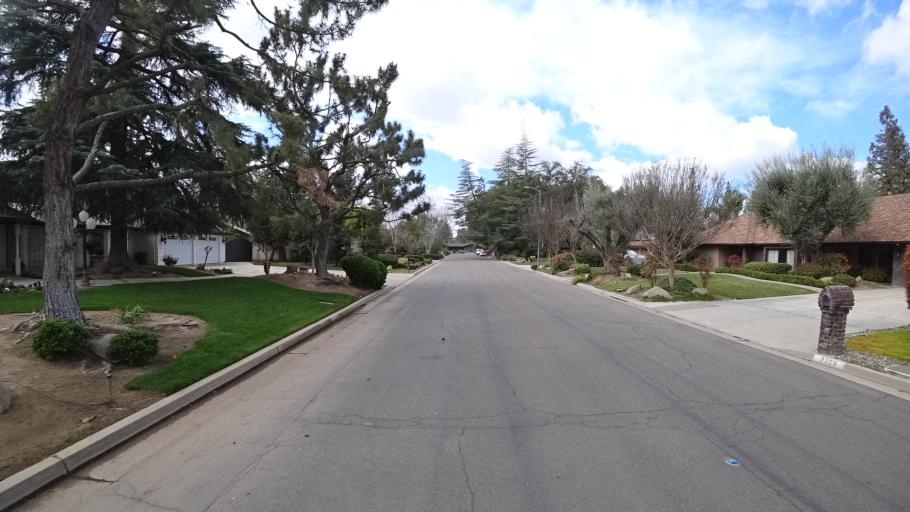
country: US
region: California
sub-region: Fresno County
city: Fresno
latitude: 36.8292
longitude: -119.8423
